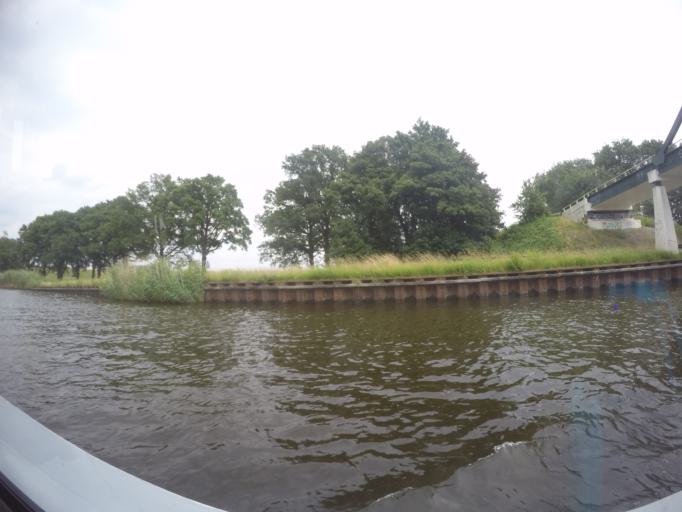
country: NL
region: Overijssel
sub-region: Gemeente Almelo
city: Almelo
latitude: 52.3235
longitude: 6.6292
